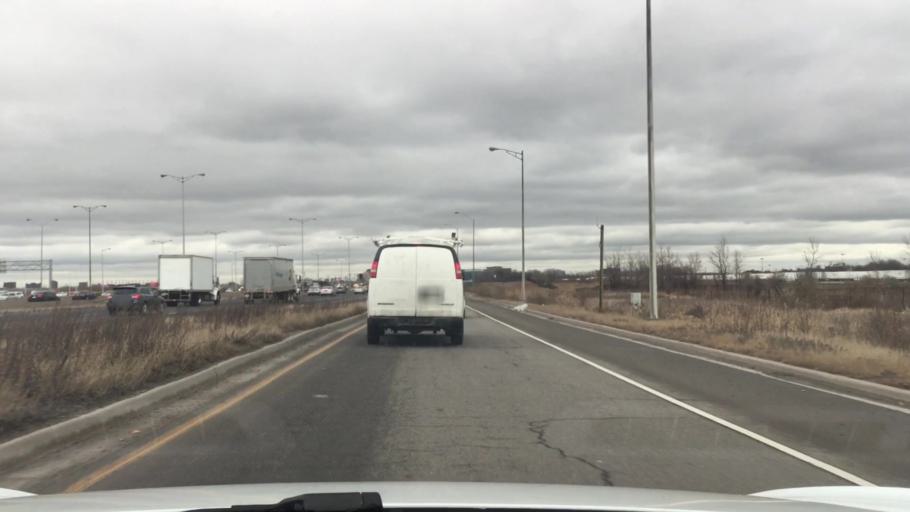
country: CA
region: Ontario
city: Etobicoke
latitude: 43.6488
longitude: -79.6343
